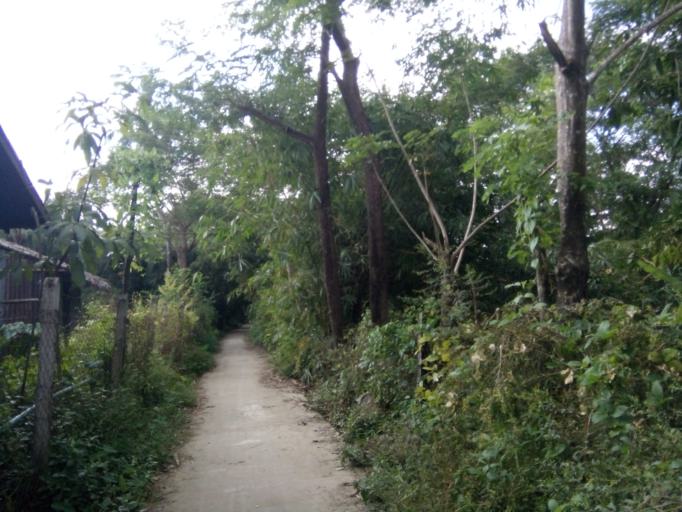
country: MM
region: Yangon
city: Kanbe
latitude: 16.8732
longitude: 95.9804
